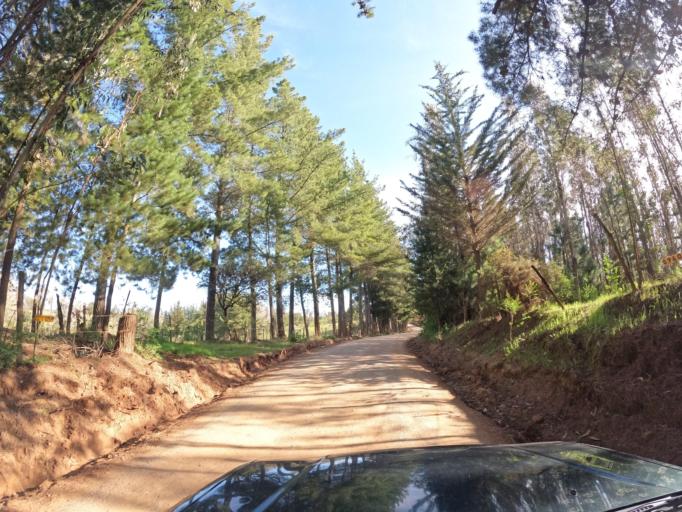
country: CL
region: Biobio
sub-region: Provincia de Biobio
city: La Laja
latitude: -37.1392
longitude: -72.7281
